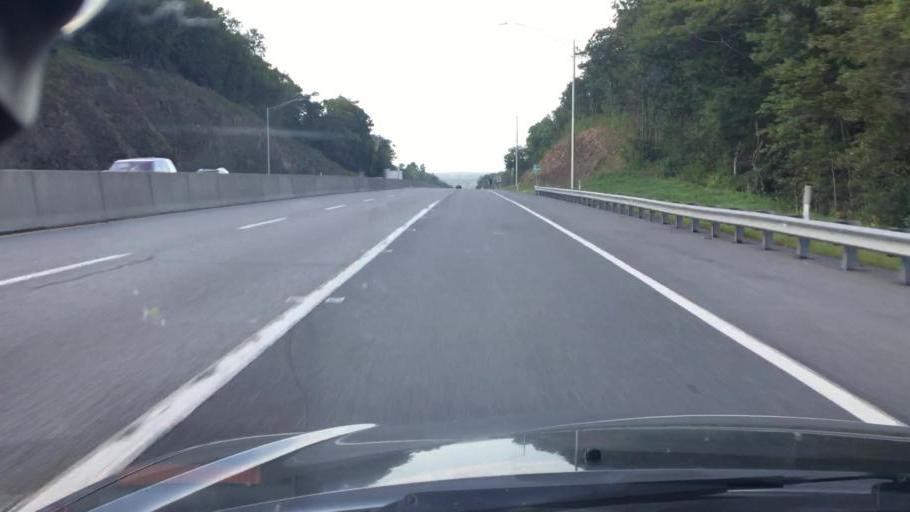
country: US
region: Pennsylvania
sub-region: Carbon County
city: Towamensing Trails
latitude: 40.9869
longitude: -75.6304
